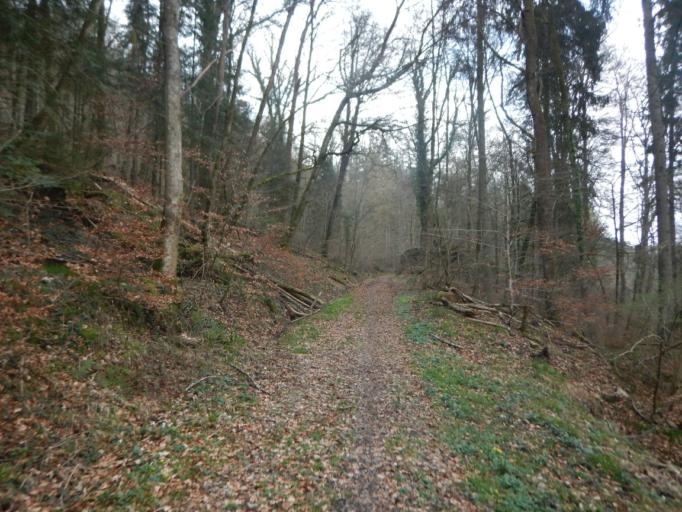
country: LU
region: Grevenmacher
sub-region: Canton d'Echternach
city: Beaufort
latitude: 49.8399
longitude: 6.3181
